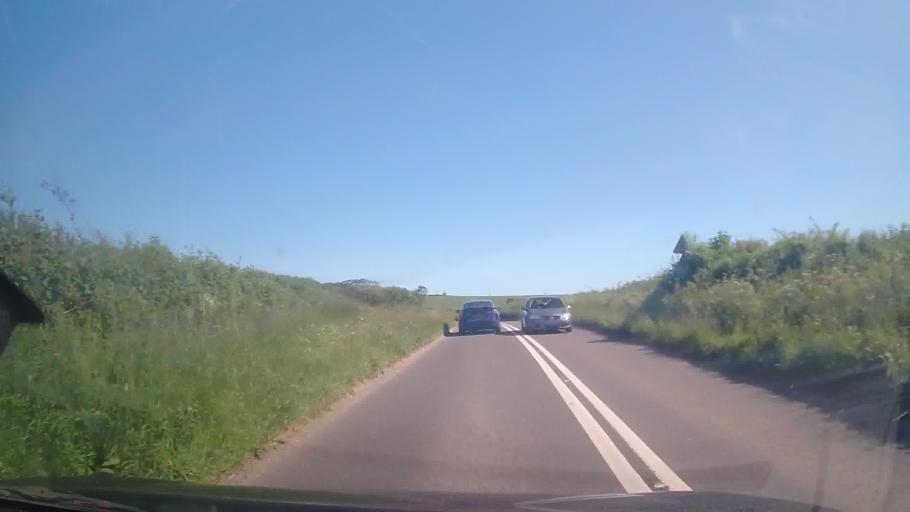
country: GB
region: England
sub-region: Devon
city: Dartmouth
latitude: 50.3820
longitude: -3.5590
